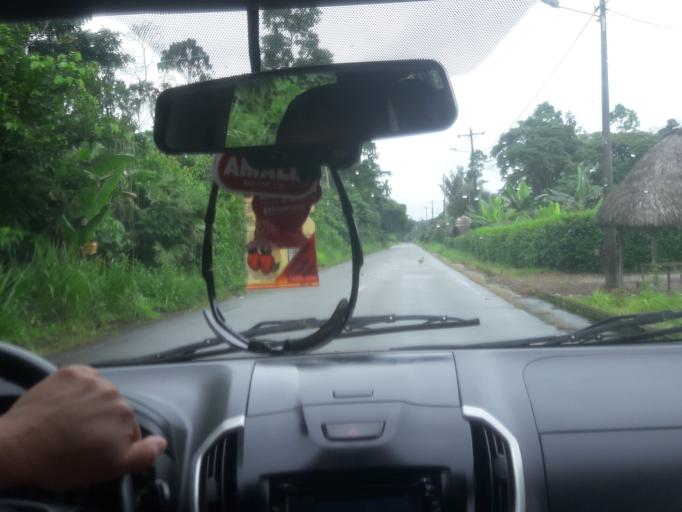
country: EC
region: Napo
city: Tena
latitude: -1.0383
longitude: -77.6917
